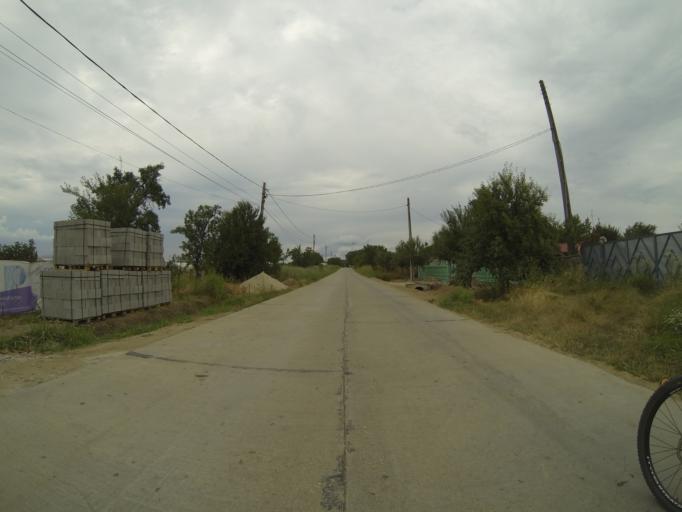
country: RO
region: Dolj
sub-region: Comuna Almaju
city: Almaju
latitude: 44.4385
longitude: 23.7039
